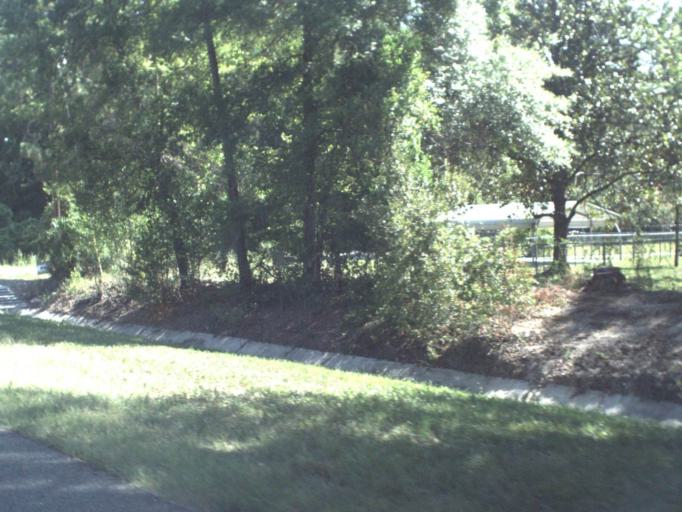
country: US
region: Florida
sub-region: Alachua County
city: Waldo
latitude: 29.7236
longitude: -82.1410
